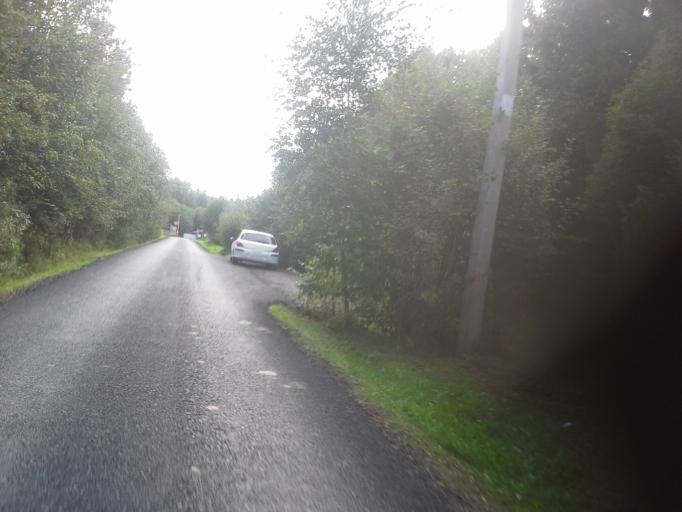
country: RU
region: Moskovskaya
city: Kievskij
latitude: 55.4502
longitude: 36.8632
